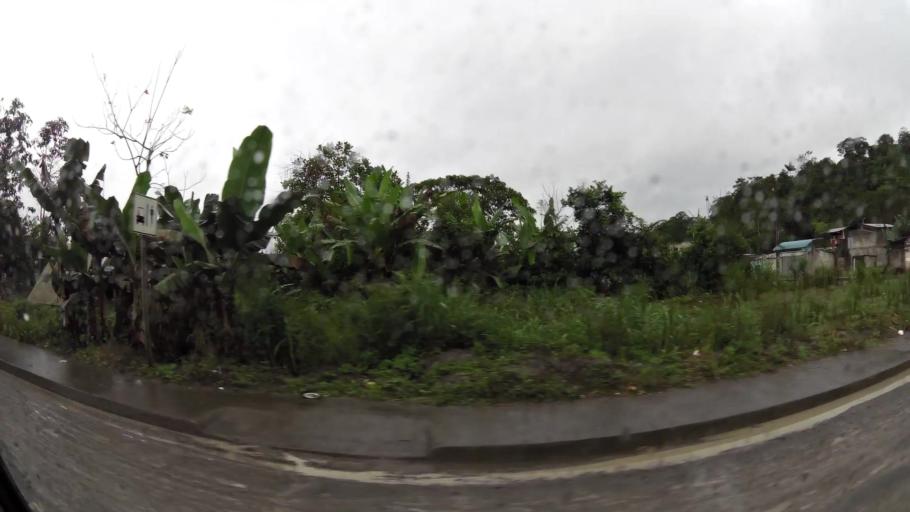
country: EC
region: Santo Domingo de los Tsachilas
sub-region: Canton Santo Domingo de los Colorados
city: Santo Domingo de los Colorados
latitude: -0.2431
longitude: -79.1359
